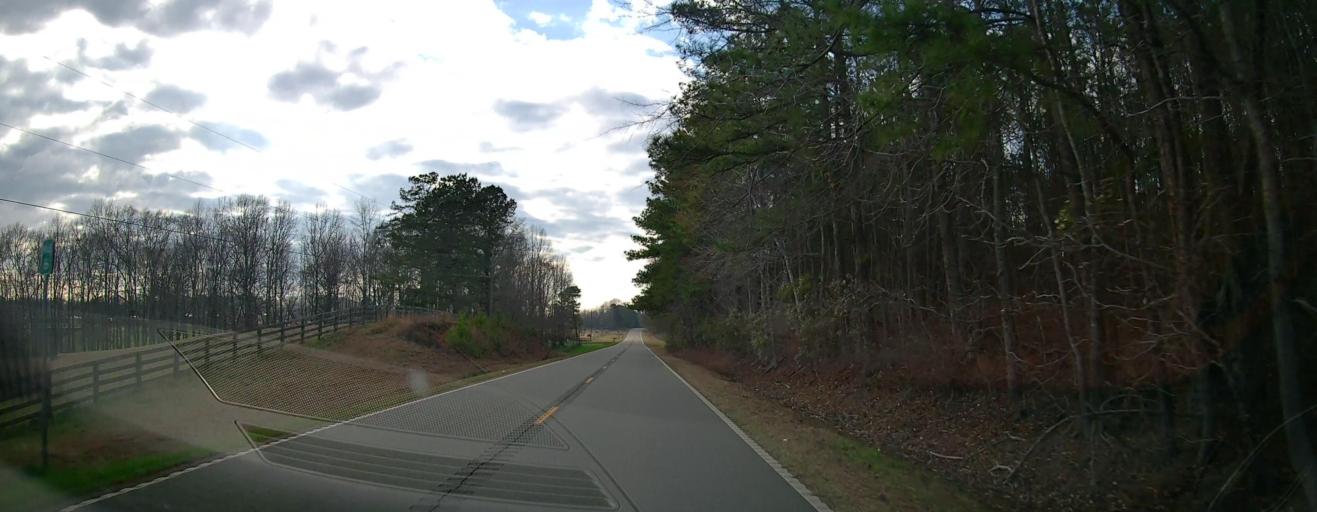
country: US
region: Georgia
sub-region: Harris County
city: Hamilton
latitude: 32.6846
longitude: -84.7616
